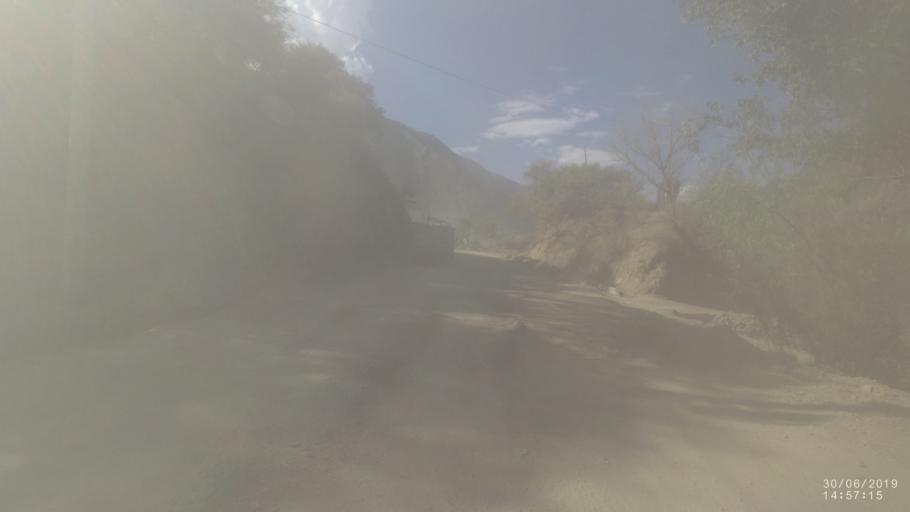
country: BO
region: Cochabamba
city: Irpa Irpa
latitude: -17.7444
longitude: -66.3536
